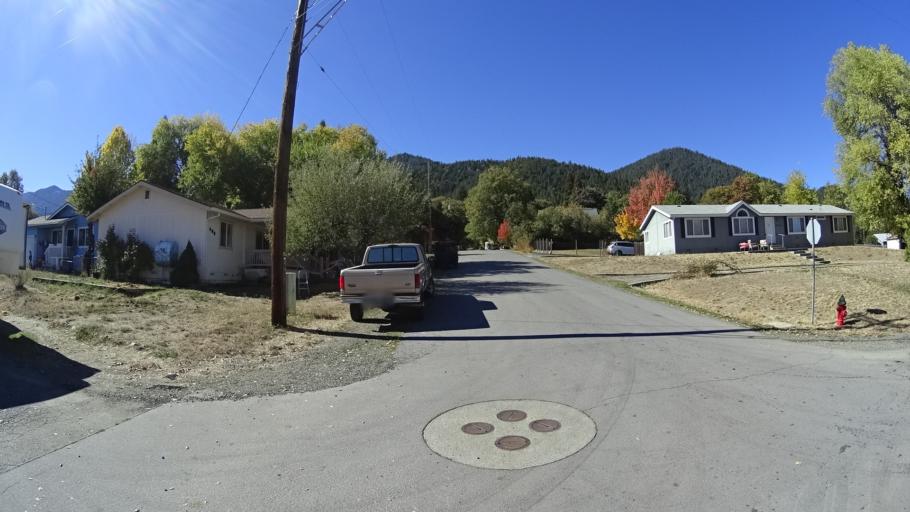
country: US
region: California
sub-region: Siskiyou County
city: Yreka
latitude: 41.4545
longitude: -122.9007
